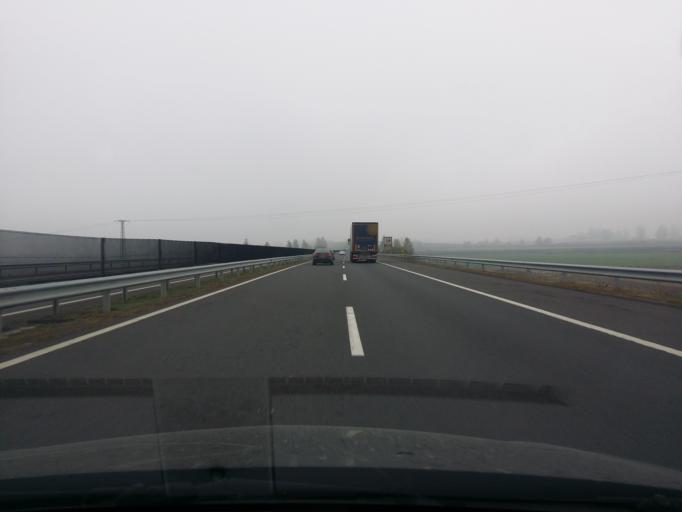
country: HU
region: Hajdu-Bihar
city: Hajdunanas
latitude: 47.8723
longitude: 21.3805
